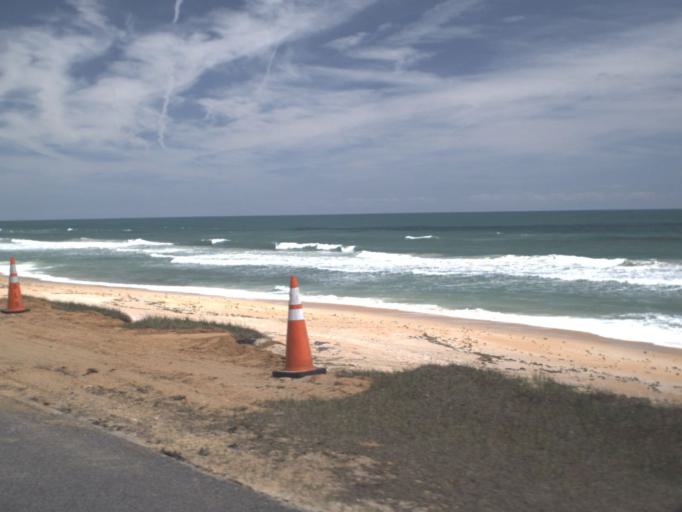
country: US
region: Florida
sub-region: Flagler County
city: Flagler Beach
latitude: 29.5067
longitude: -81.1399
